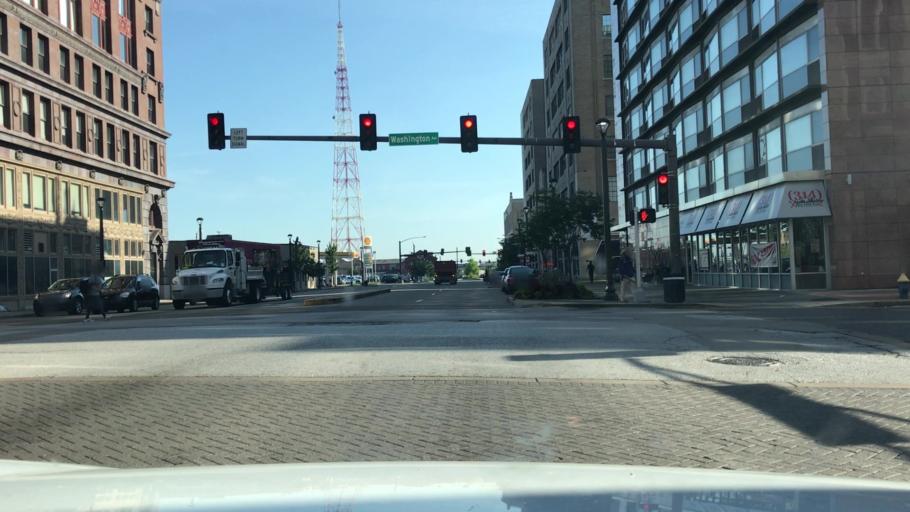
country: US
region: Missouri
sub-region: City of Saint Louis
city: St. Louis
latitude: 38.6317
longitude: -90.1967
